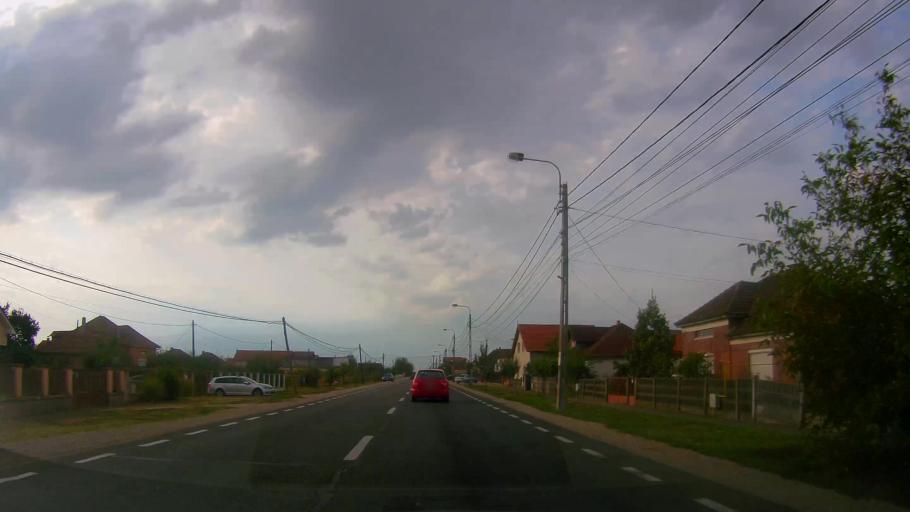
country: RO
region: Satu Mare
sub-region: Oras Ardud
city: Madaras
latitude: 47.7345
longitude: 22.8825
